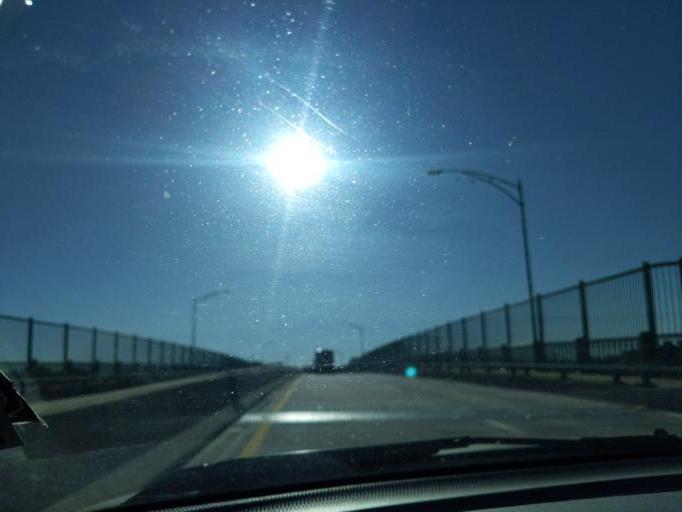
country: US
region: Massachusetts
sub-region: Essex County
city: Gloucester
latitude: 42.6254
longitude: -70.6893
